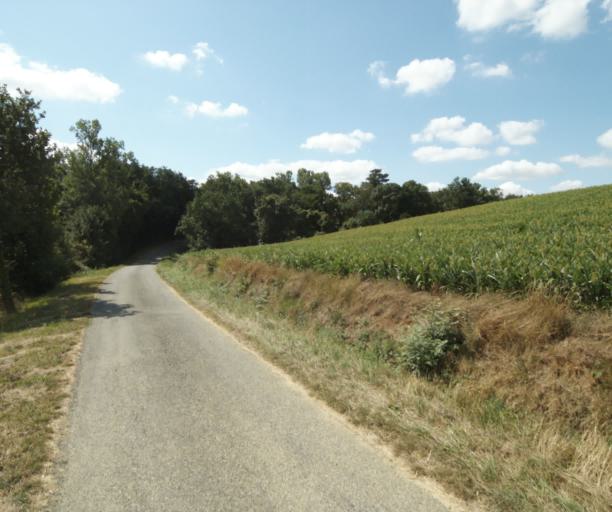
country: FR
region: Midi-Pyrenees
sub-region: Departement de la Haute-Garonne
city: Auriac-sur-Vendinelle
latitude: 43.4622
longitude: 1.8010
